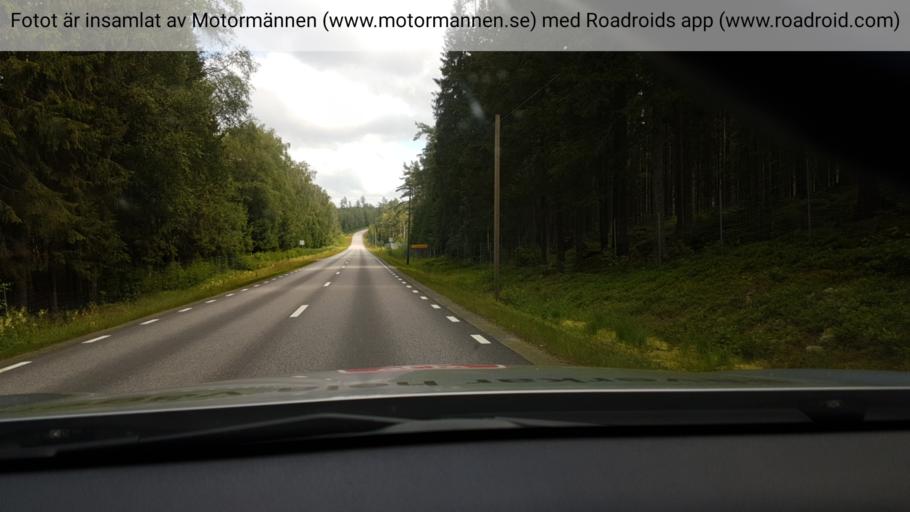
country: SE
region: Vaestra Goetaland
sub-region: Marks Kommun
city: Fritsla
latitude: 57.4838
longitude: 12.8240
